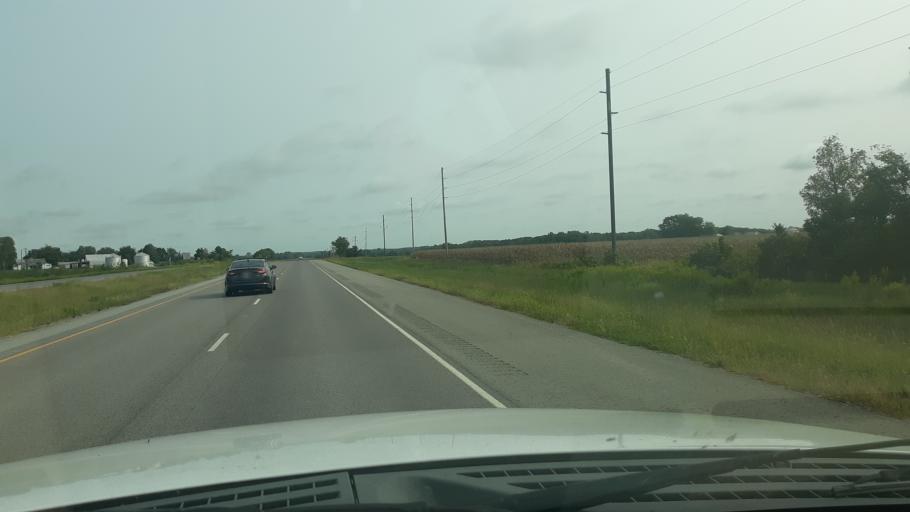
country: US
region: Illinois
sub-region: Saline County
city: Eldorado
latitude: 37.8543
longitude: -88.4074
